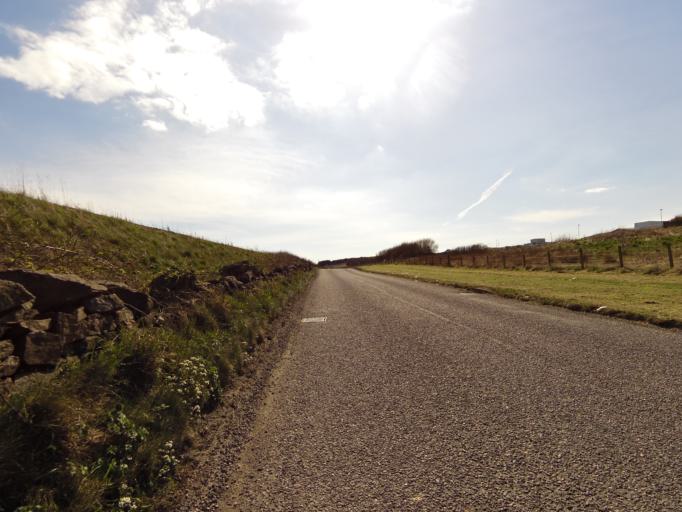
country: GB
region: Scotland
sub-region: Aberdeen City
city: Aberdeen
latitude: 57.1154
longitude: -2.0640
